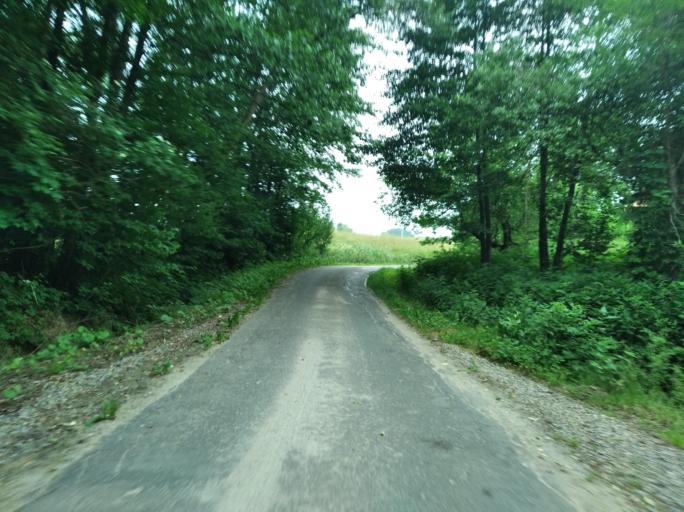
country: PL
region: Subcarpathian Voivodeship
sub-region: Powiat brzozowski
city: Jasienica Rosielna
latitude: 49.7570
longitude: 21.9240
